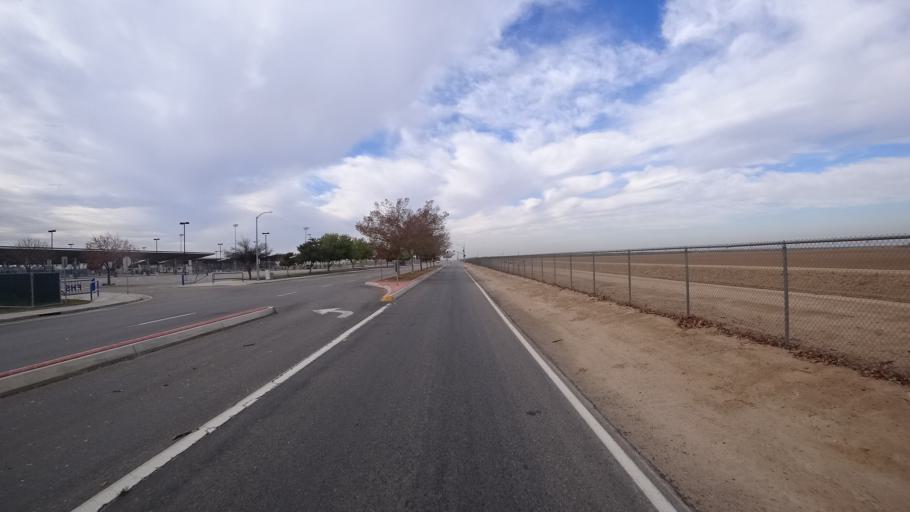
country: US
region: California
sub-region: Kern County
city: Rosedale
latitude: 35.4198
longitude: -119.1482
